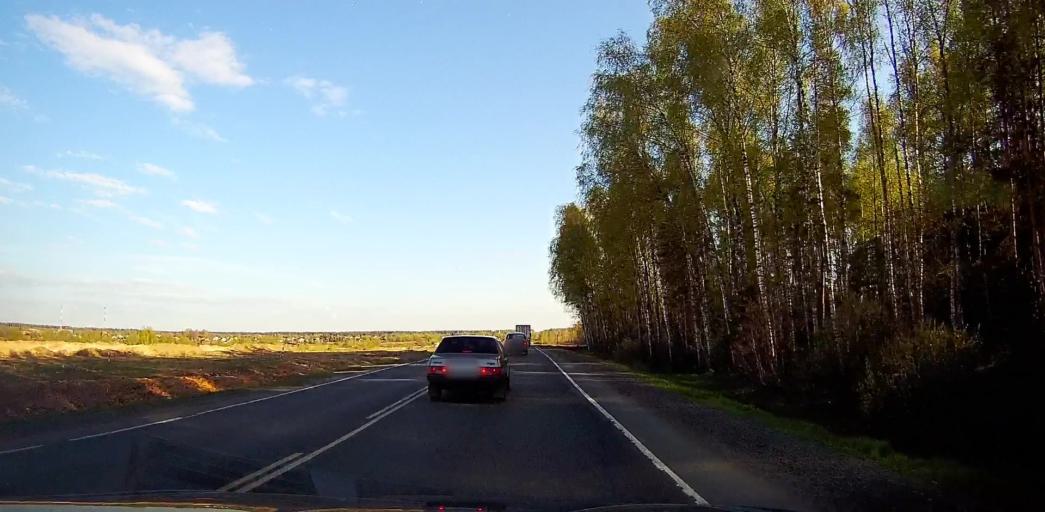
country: RU
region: Moskovskaya
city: Gzhel'
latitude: 55.5858
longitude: 38.3848
